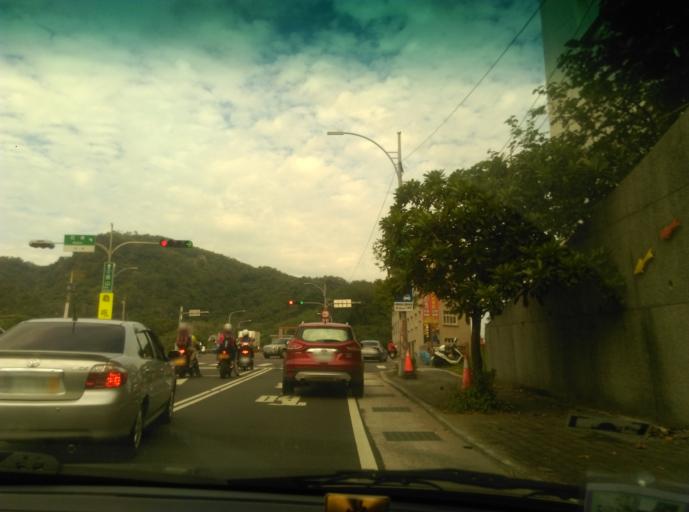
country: TW
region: Taiwan
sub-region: Keelung
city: Keelung
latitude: 25.1911
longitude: 121.6835
